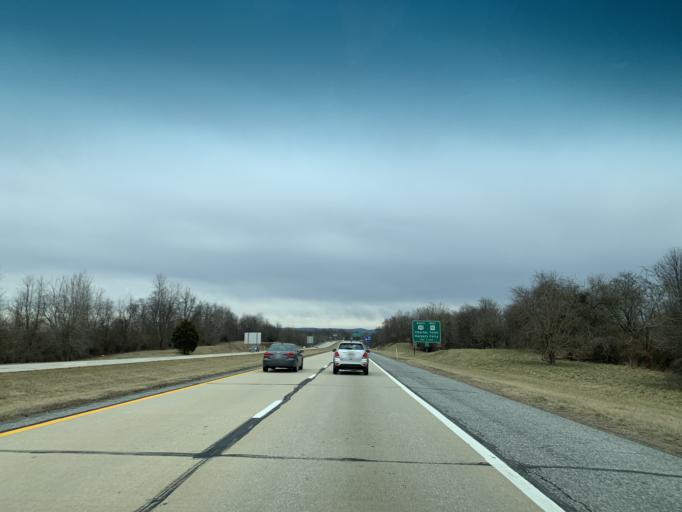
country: US
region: West Virginia
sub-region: Jefferson County
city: Ranson
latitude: 39.3153
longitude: -77.8468
